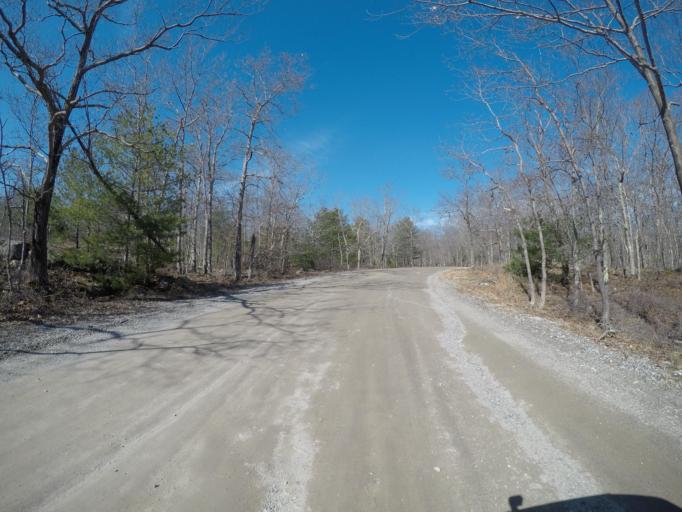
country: US
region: Massachusetts
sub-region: Norfolk County
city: Sharon
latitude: 42.0814
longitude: -71.1503
